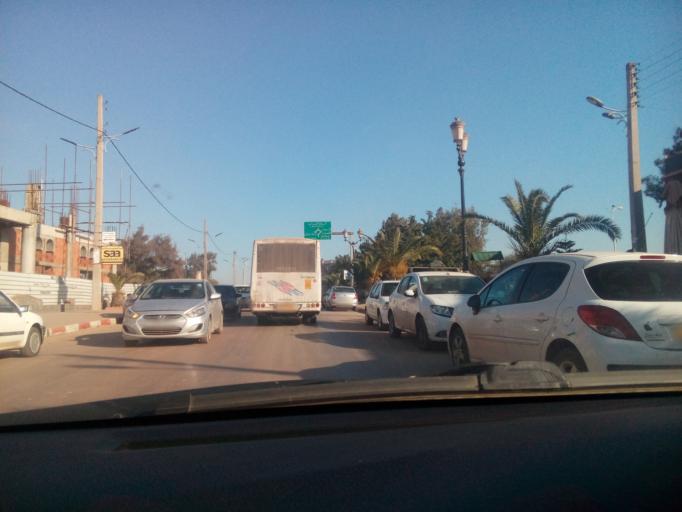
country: DZ
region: Oran
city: Es Senia
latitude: 35.6488
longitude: -0.6138
